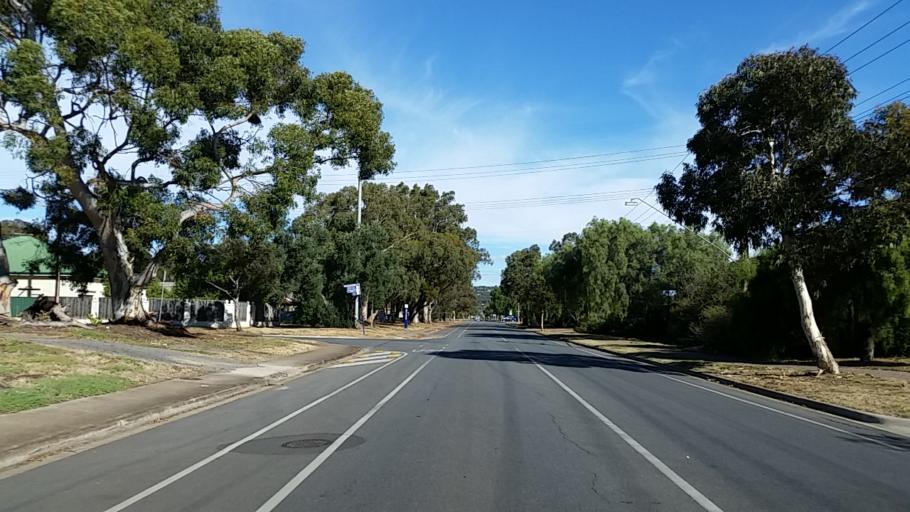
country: AU
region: South Australia
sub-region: Salisbury
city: Salisbury
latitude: -34.7781
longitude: 138.6460
